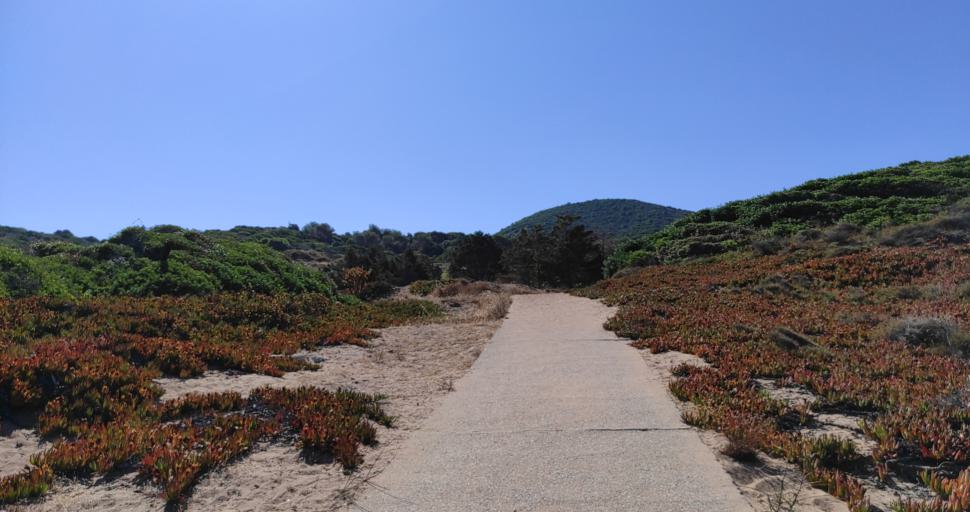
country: FR
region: Corsica
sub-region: Departement de la Corse-du-Sud
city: Alata
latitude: 41.9849
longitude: 8.6702
